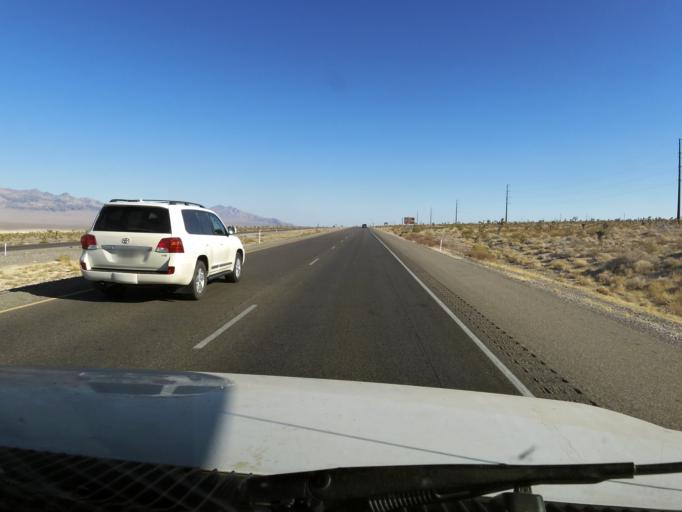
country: US
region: Nevada
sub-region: Clark County
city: Summerlin South
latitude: 36.4823
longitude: -115.4768
